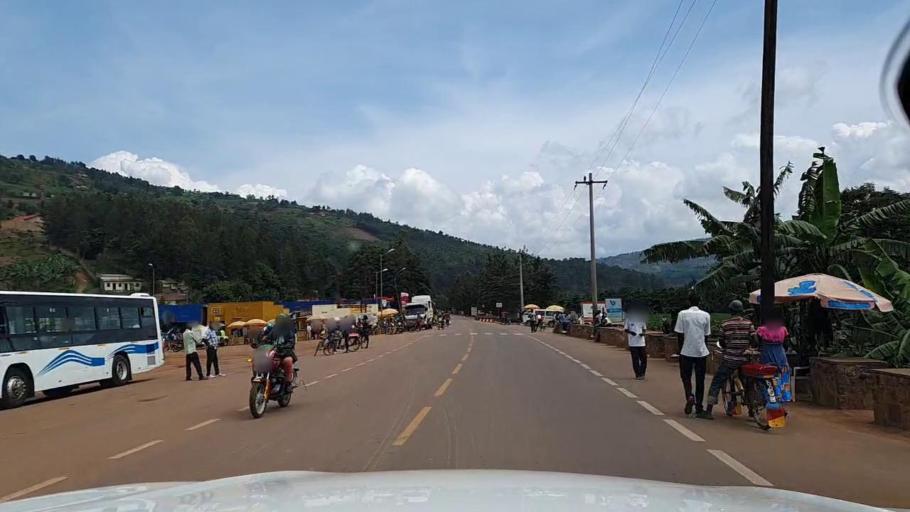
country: RW
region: Kigali
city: Kigali
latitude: -1.8670
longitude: 30.0868
